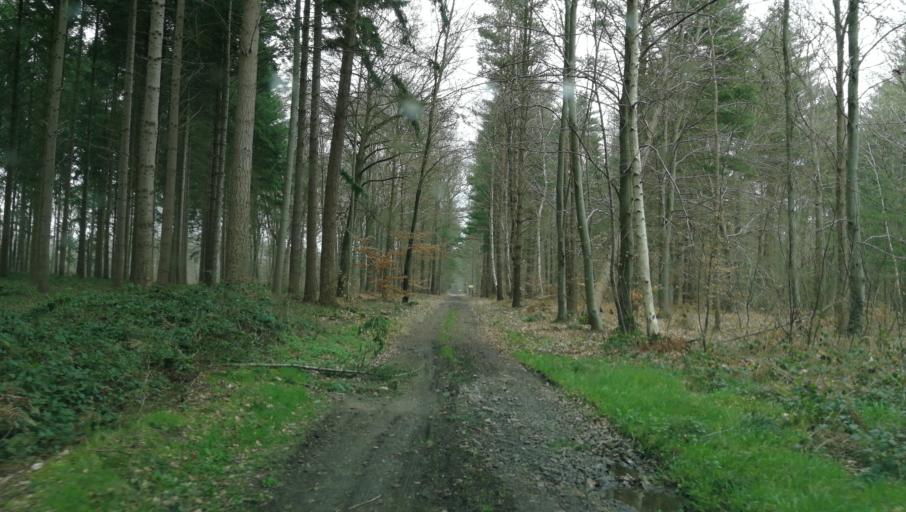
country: FR
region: Haute-Normandie
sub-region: Departement de l'Eure
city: Brionne
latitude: 49.1843
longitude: 0.6977
